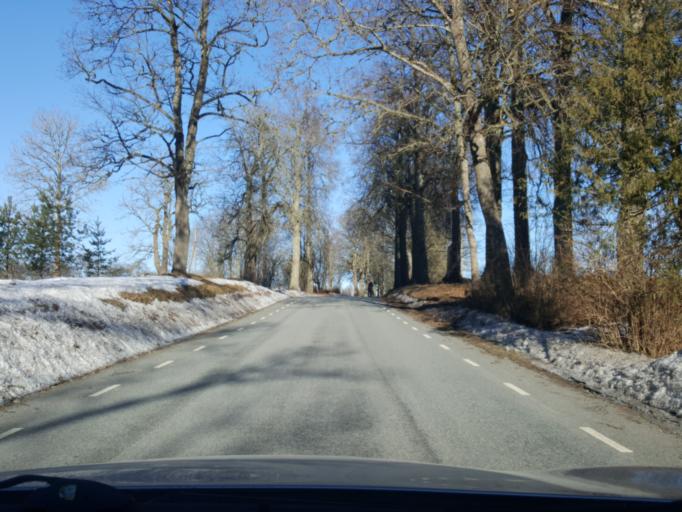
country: EE
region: Viljandimaa
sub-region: Vohma linn
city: Vohma
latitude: 58.5309
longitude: 25.5842
